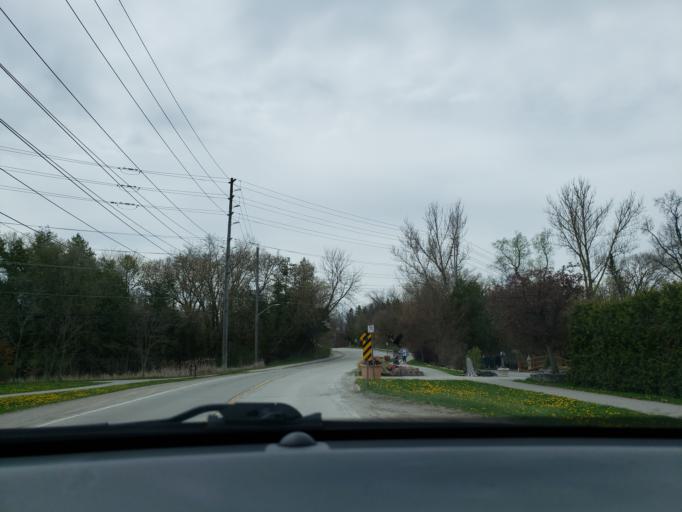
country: CA
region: Ontario
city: Newmarket
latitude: 44.0664
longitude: -79.4571
